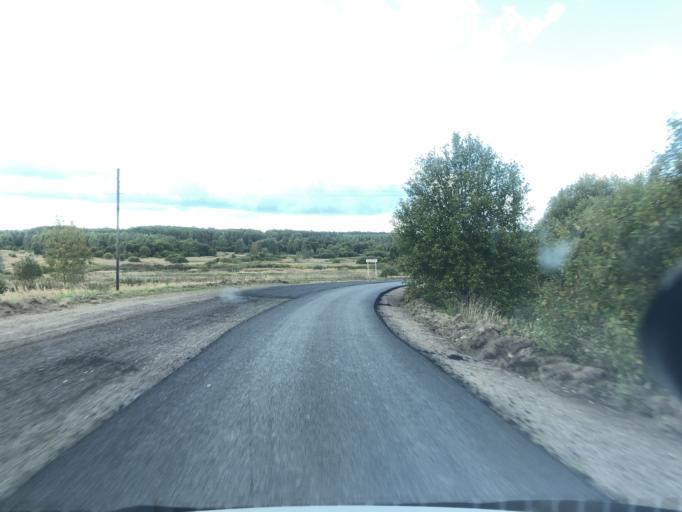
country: RU
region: Jaroslavl
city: Porech'ye-Rybnoye
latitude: 56.9589
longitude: 39.4847
